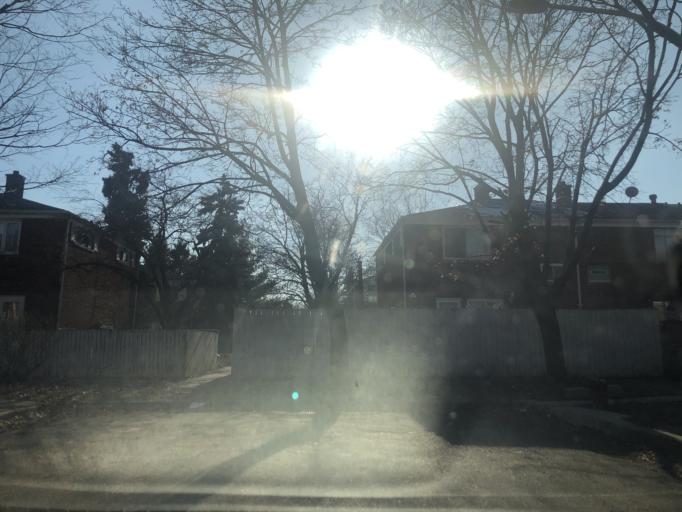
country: US
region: Illinois
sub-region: Cook County
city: Evanston
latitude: 42.0183
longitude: -87.6865
